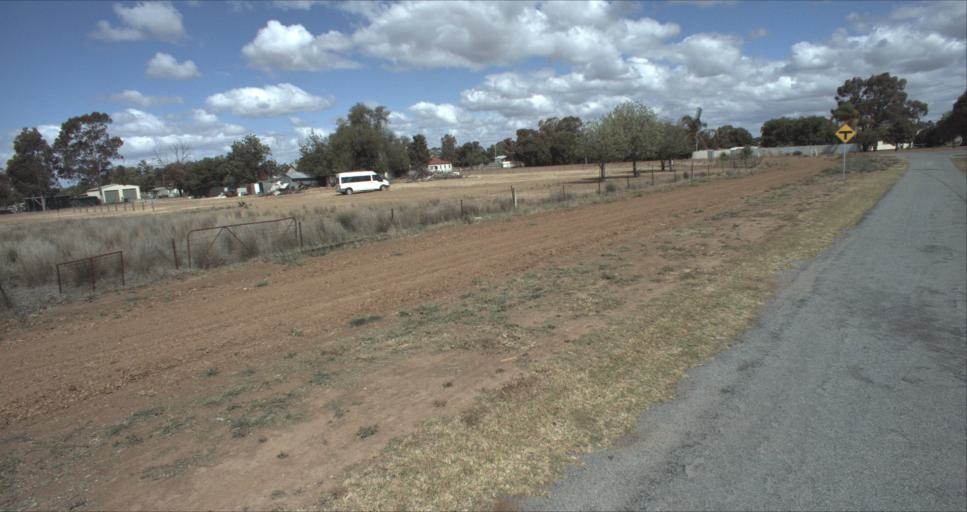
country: AU
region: New South Wales
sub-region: Leeton
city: Leeton
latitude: -34.5932
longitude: 146.4090
